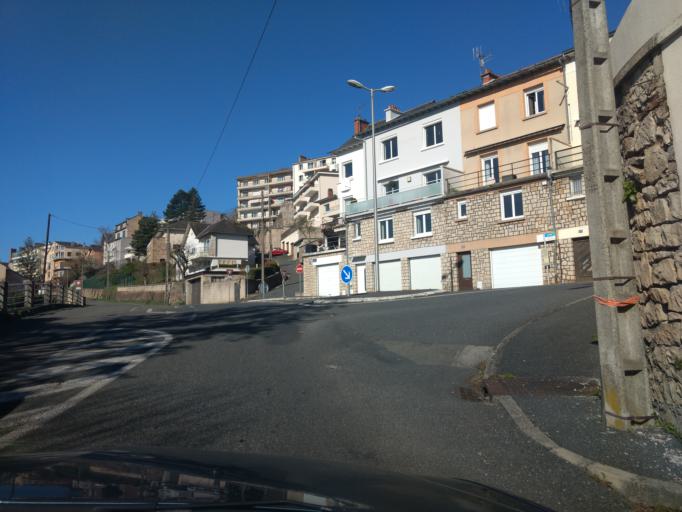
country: FR
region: Midi-Pyrenees
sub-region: Departement de l'Aveyron
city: Le Monastere
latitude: 44.3456
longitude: 2.5769
